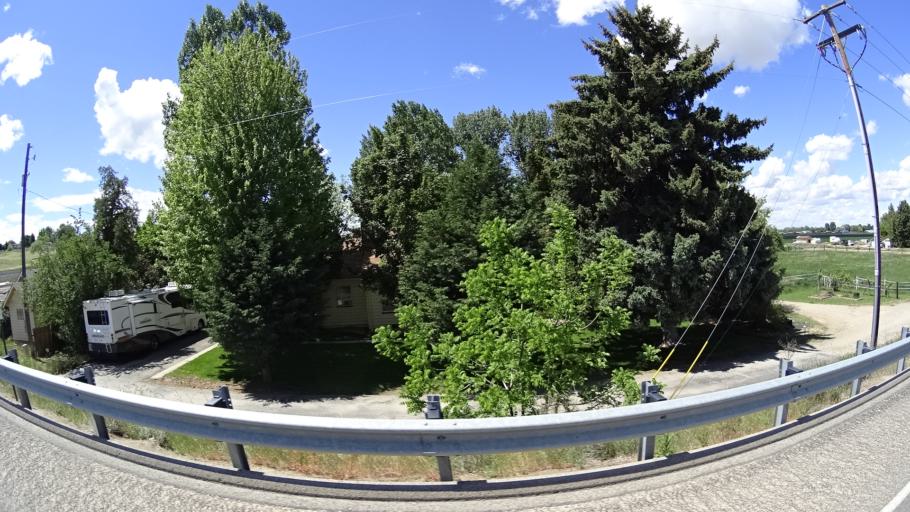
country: US
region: Idaho
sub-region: Ada County
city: Meridian
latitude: 43.5964
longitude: -116.4537
